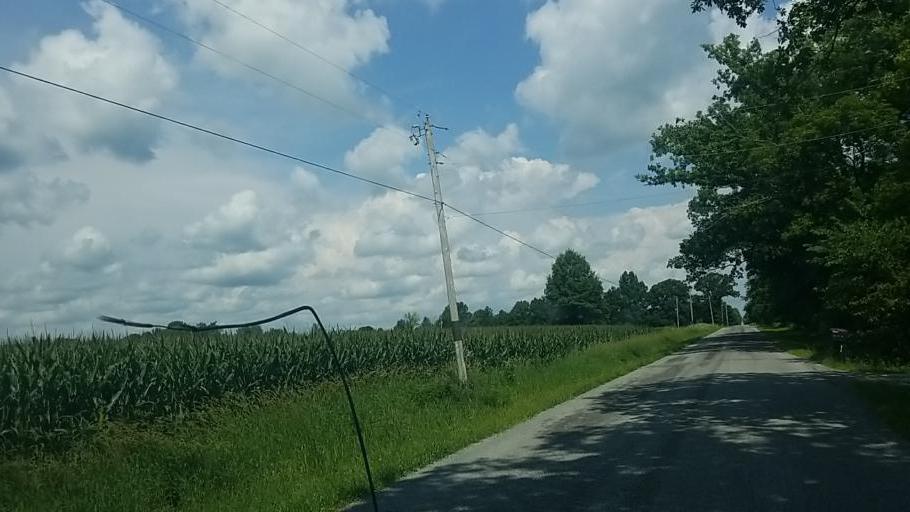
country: US
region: Ohio
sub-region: Wayne County
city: West Salem
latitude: 41.0069
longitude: -82.0781
